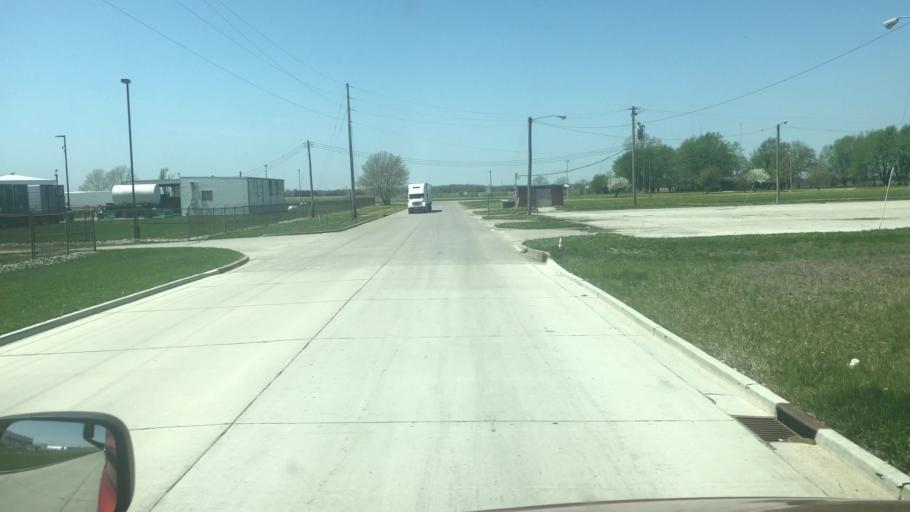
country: US
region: Missouri
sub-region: Adair County
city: Kirksville
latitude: 40.2210
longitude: -92.5892
